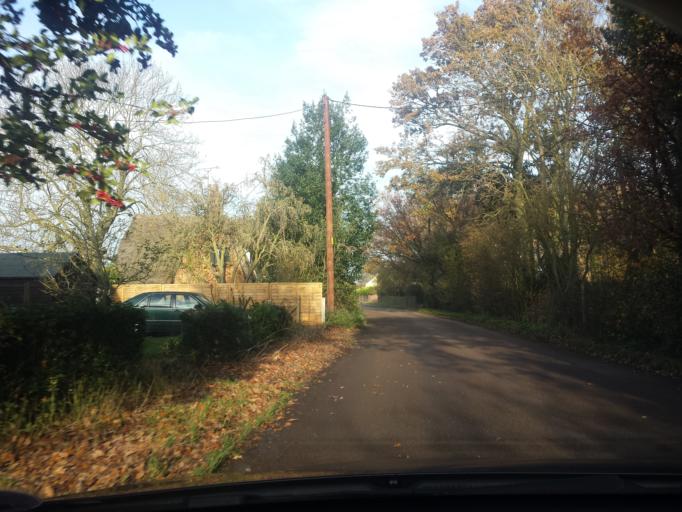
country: GB
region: England
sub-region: Essex
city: Little Clacton
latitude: 51.8349
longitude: 1.1203
